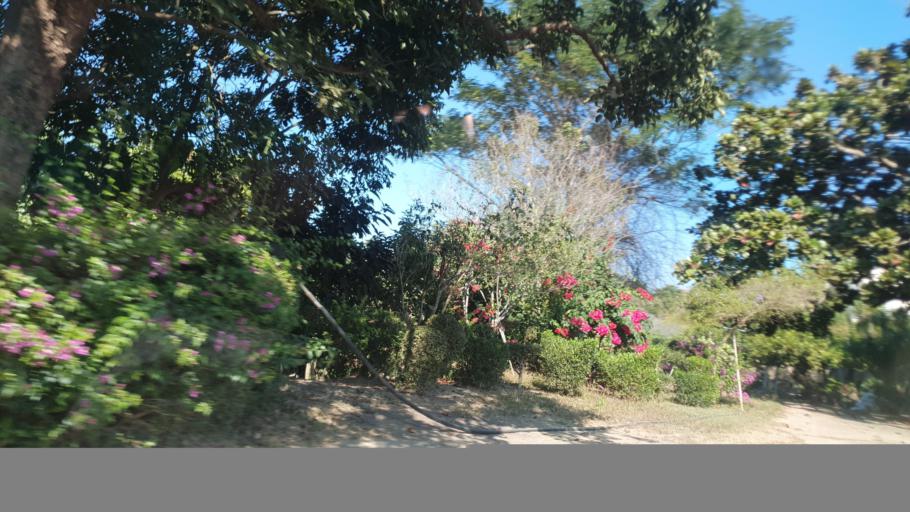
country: TW
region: Taiwan
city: Yujing
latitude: 23.0474
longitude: 120.3777
